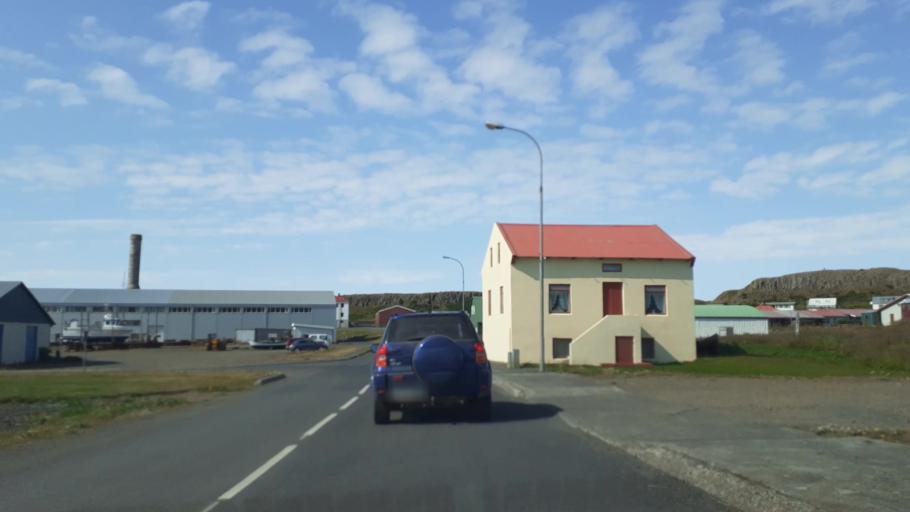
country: IS
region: Northwest
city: Saudarkrokur
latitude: 65.8270
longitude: -20.3135
